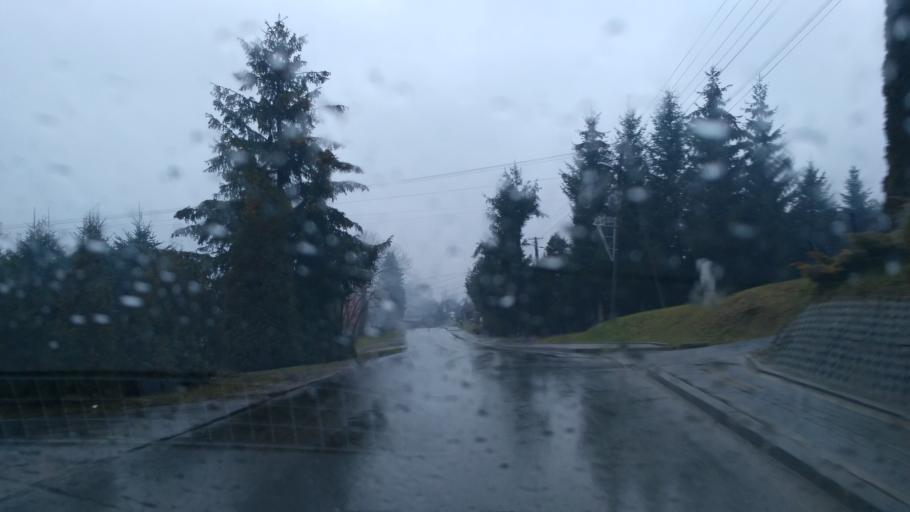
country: PL
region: Subcarpathian Voivodeship
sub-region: Powiat krosnienski
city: Kroscienko Wyzne
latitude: 49.6802
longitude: 21.8250
